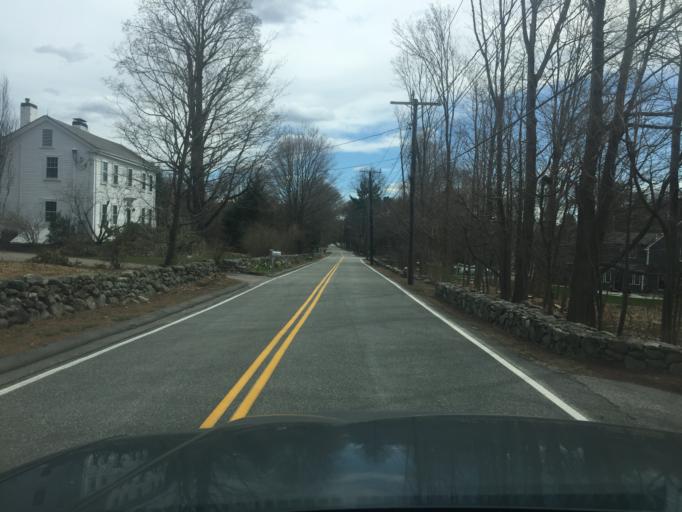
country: US
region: Massachusetts
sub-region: Norfolk County
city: Medfield
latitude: 42.2151
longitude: -71.3181
